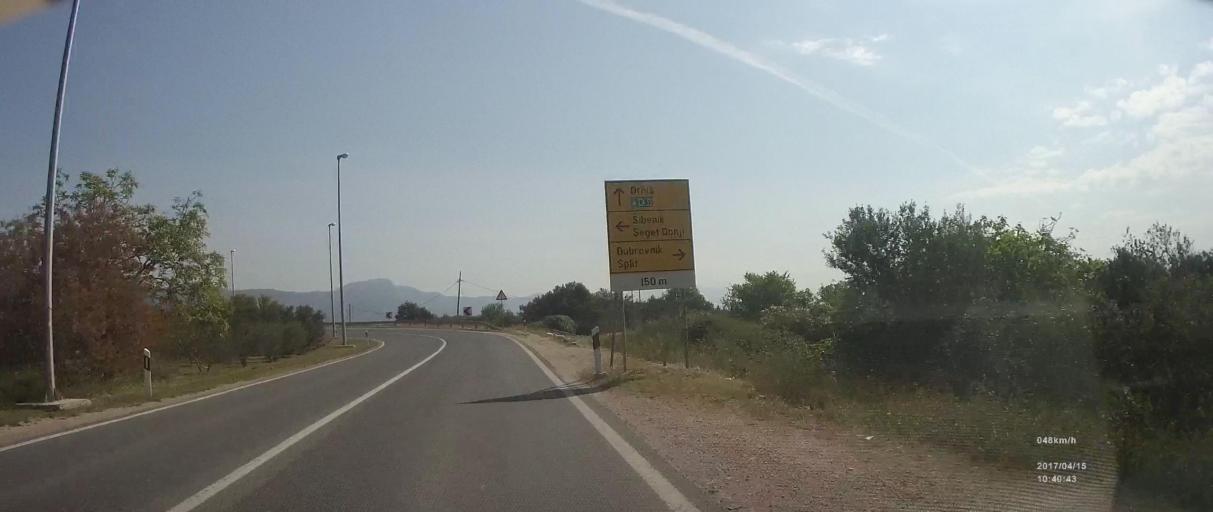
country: HR
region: Splitsko-Dalmatinska
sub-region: Grad Trogir
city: Trogir
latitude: 43.5355
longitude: 16.2857
